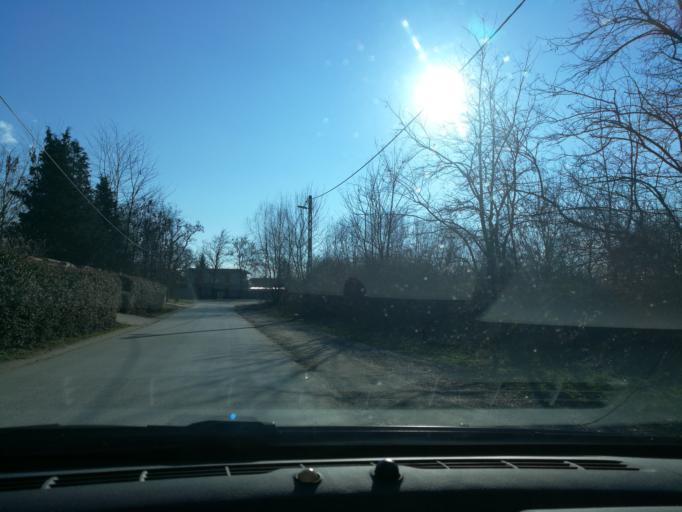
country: HU
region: Szabolcs-Szatmar-Bereg
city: Nyiregyhaza
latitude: 47.9416
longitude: 21.7265
